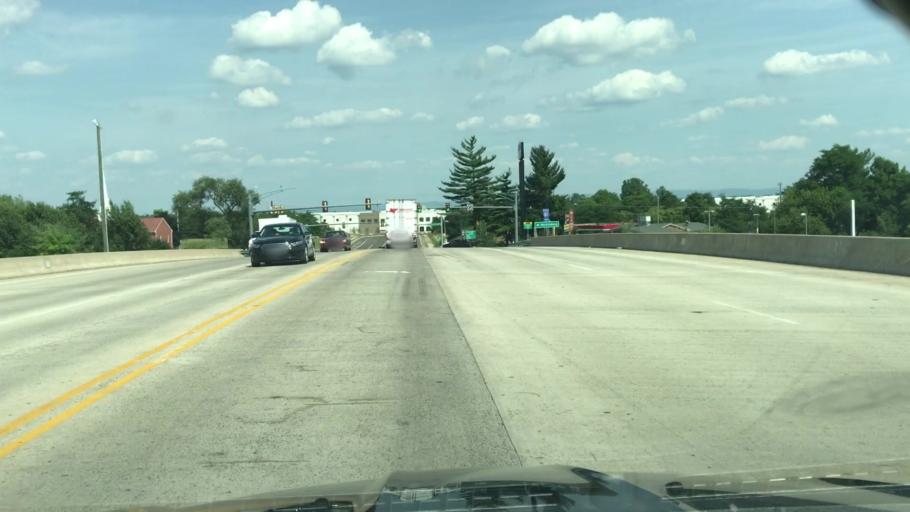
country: US
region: West Virginia
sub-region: Berkeley County
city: Inwood
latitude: 39.2910
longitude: -78.0851
